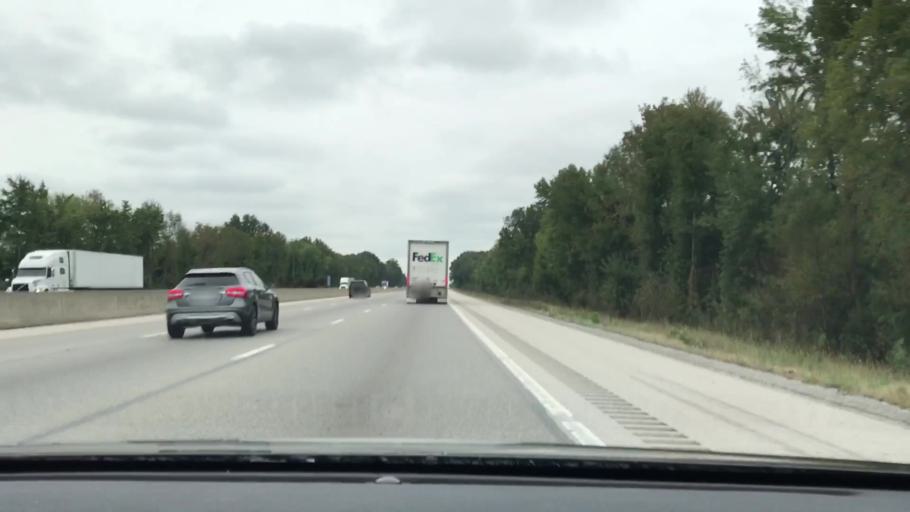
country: US
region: Kentucky
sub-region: Warren County
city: Plano
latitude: 36.8578
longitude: -86.4553
